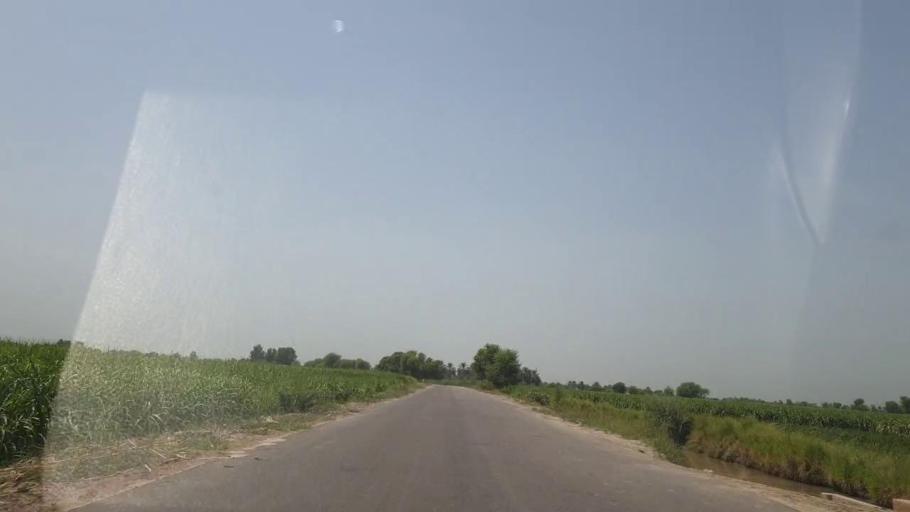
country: PK
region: Sindh
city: Ranipur
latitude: 27.2945
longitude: 68.6047
